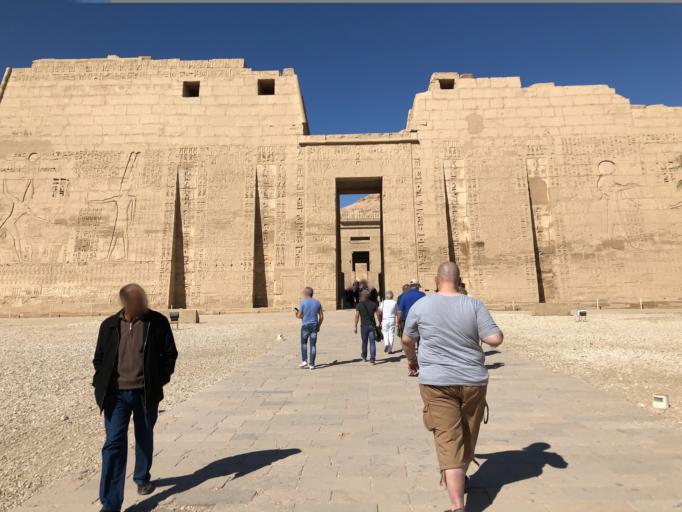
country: EG
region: Luxor
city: Luxor
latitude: 25.7191
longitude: 32.6015
